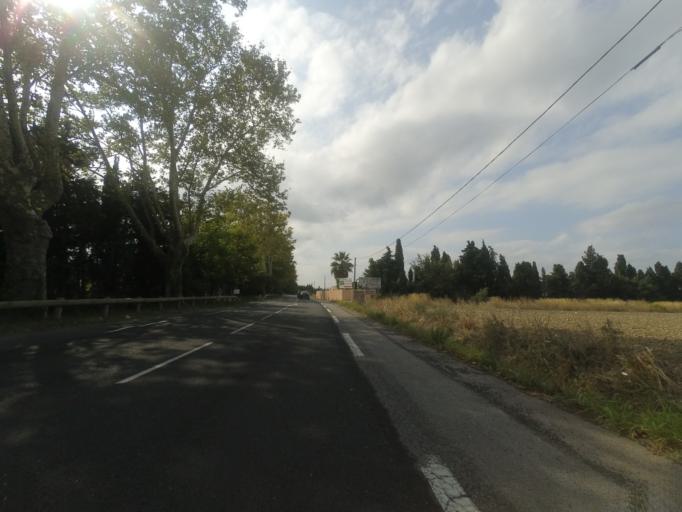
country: FR
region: Languedoc-Roussillon
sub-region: Departement des Pyrenees-Orientales
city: Toulouges
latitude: 42.6793
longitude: 2.8189
